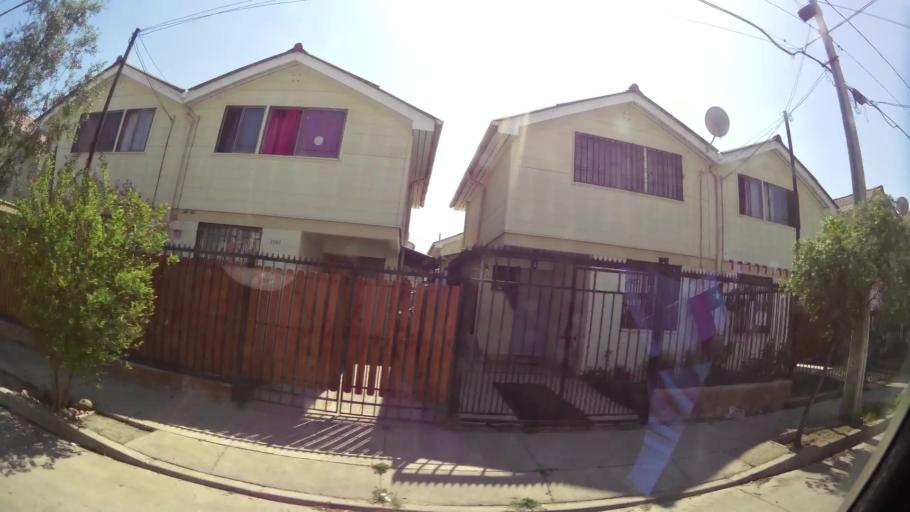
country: CL
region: Santiago Metropolitan
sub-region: Provincia de Talagante
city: Penaflor
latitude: -33.5758
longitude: -70.8033
